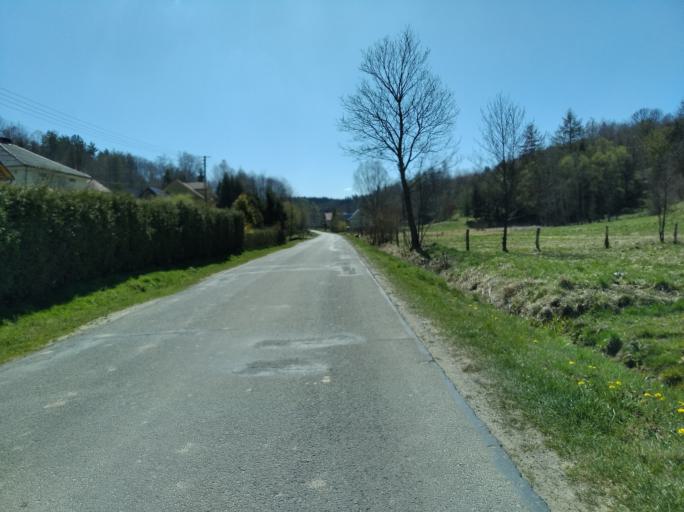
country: PL
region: Subcarpathian Voivodeship
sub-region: Powiat brzozowski
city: Jablonka
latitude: 49.7340
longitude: 22.1452
